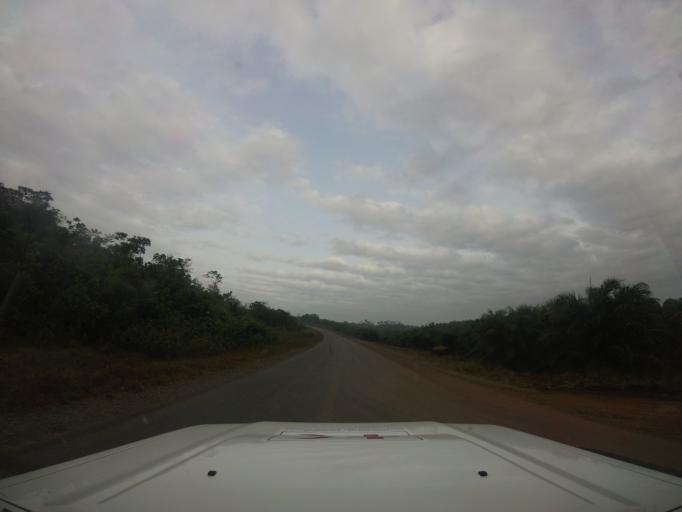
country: LR
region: Bomi
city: Tubmanburg
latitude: 6.7305
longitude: -10.9910
